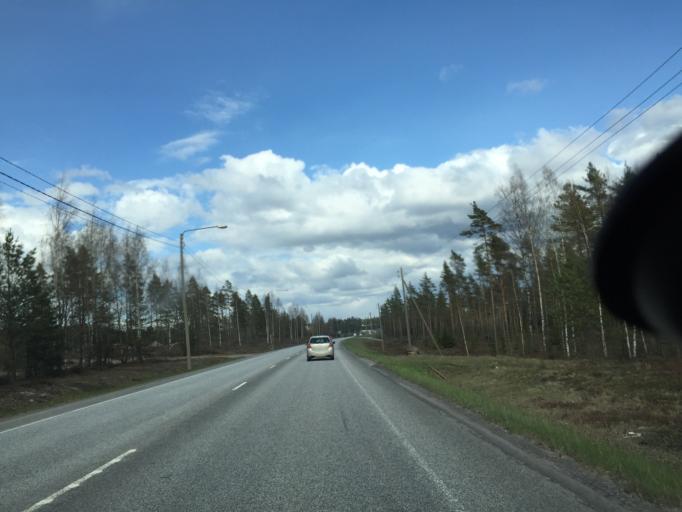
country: FI
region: Uusimaa
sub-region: Raaseporin
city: Pohja
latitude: 60.0129
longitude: 23.5536
